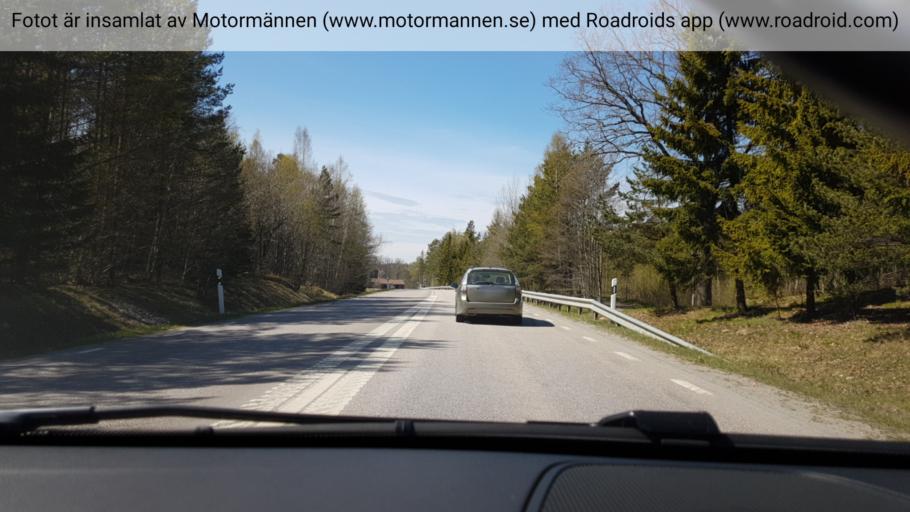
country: SE
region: Stockholm
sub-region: Nynashamns Kommun
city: Osmo
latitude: 58.9802
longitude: 17.8844
